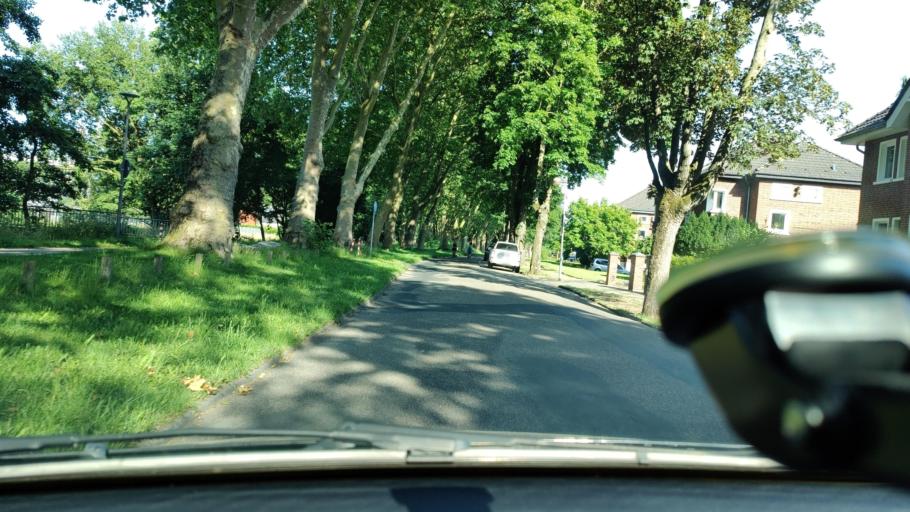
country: DE
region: North Rhine-Westphalia
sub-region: Regierungsbezirk Dusseldorf
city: Kamp-Lintfort
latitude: 51.5003
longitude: 6.5395
